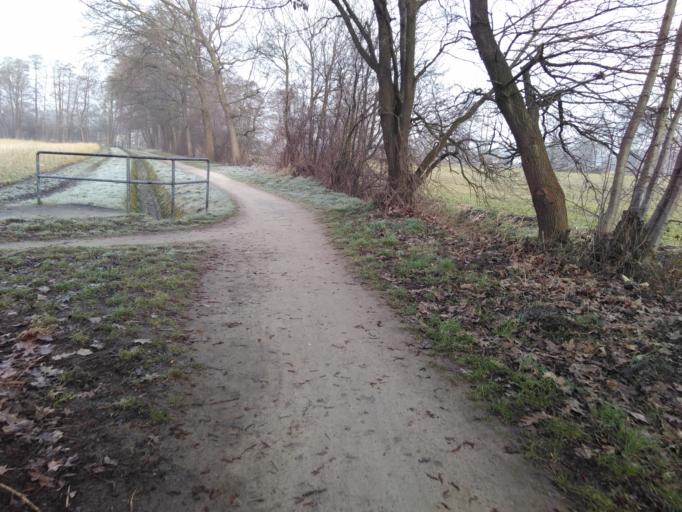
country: DE
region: North Rhine-Westphalia
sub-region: Regierungsbezirk Detmold
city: Verl
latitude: 51.8864
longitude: 8.4913
